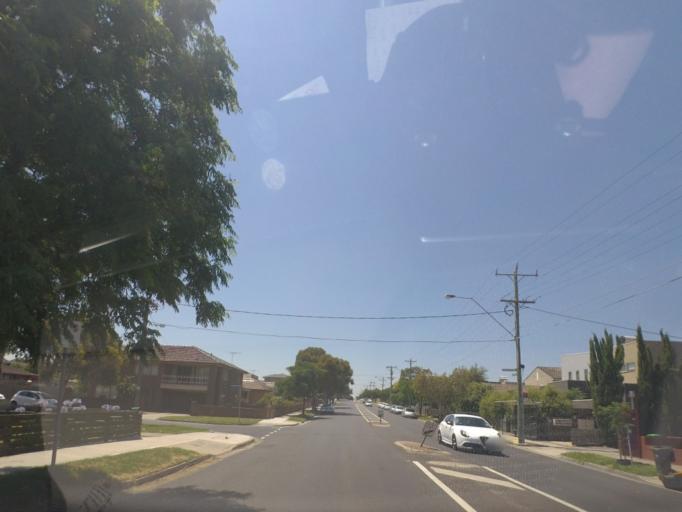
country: AU
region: Victoria
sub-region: Moreland
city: Pascoe Vale
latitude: -37.7278
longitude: 144.9390
